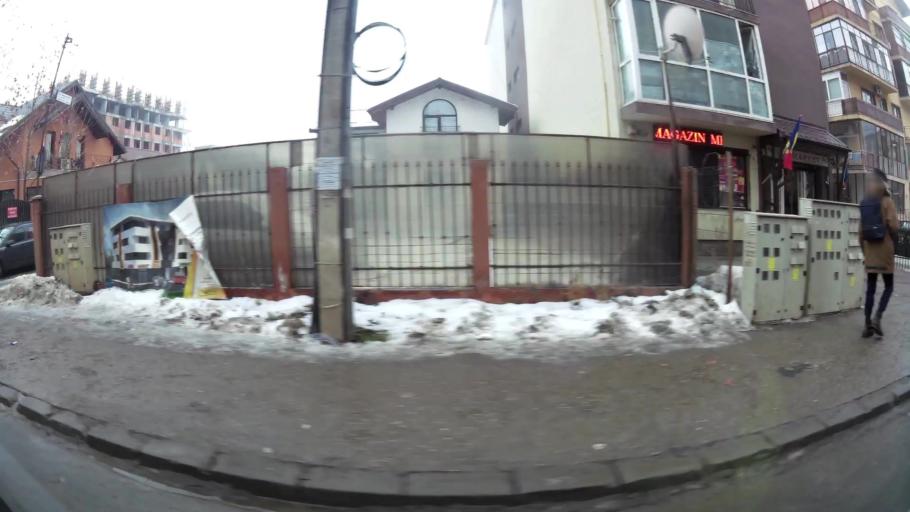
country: RO
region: Ilfov
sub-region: Comuna Chiajna
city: Chiajna
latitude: 44.4469
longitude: 25.9872
